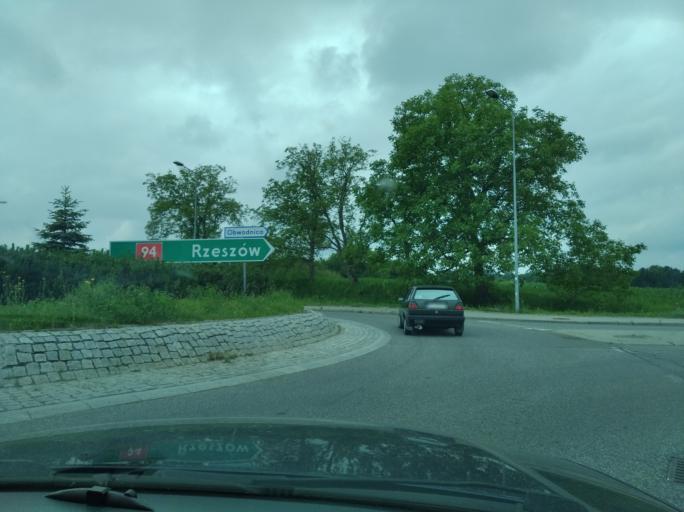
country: PL
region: Subcarpathian Voivodeship
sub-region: Powiat jaroslawski
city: Pawlosiow
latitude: 50.0251
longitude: 22.6376
